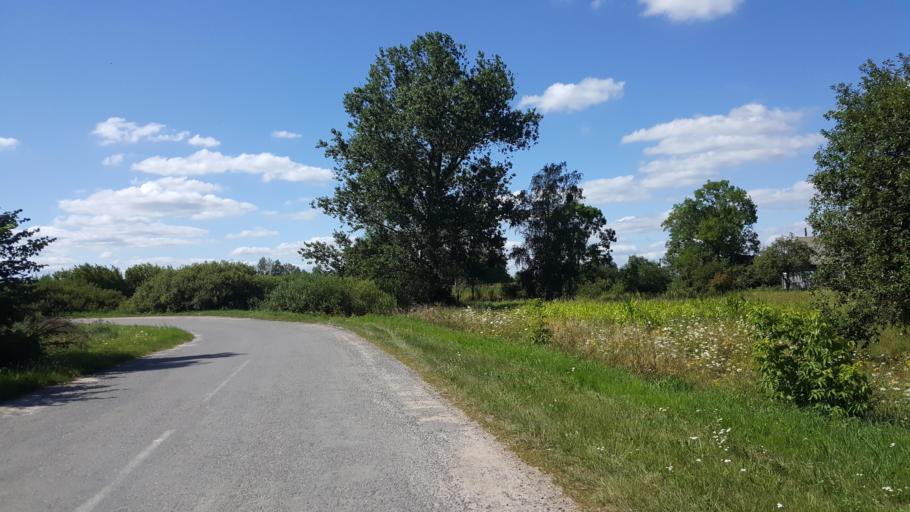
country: BY
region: Brest
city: Kobryn
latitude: 52.3157
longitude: 24.3015
